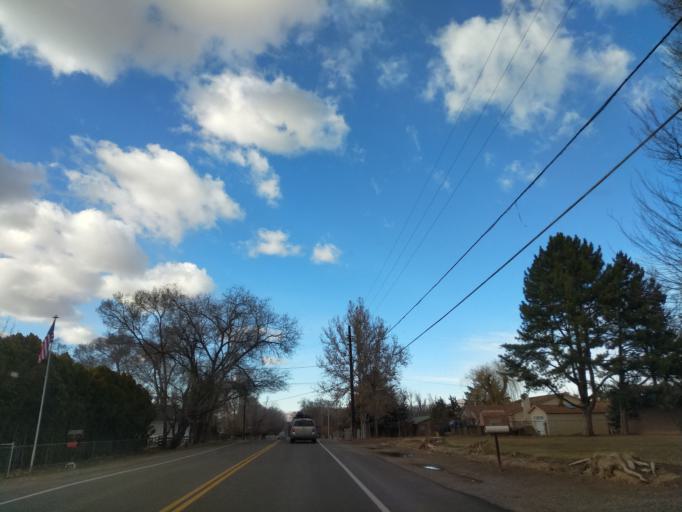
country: US
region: Colorado
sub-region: Mesa County
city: Grand Junction
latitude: 39.0949
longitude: -108.5708
